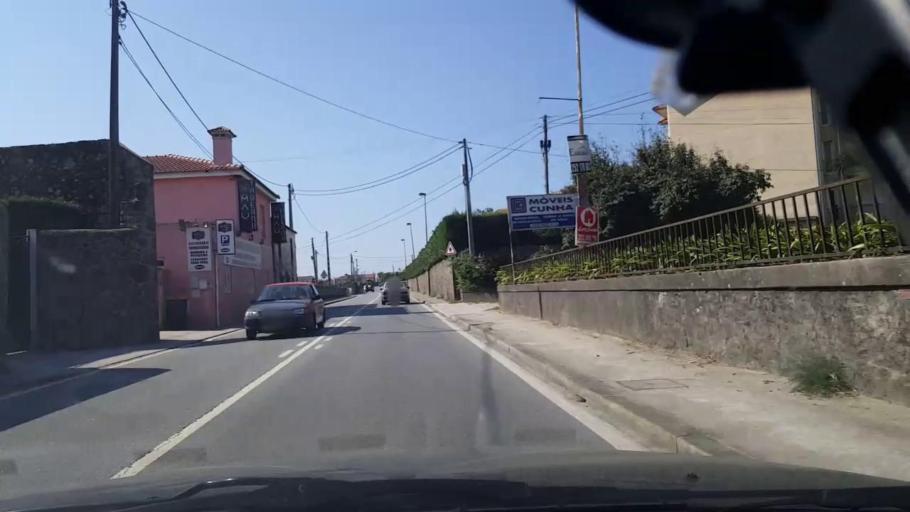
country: PT
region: Porto
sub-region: Povoa de Varzim
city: Pedroso
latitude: 41.3961
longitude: -8.6877
